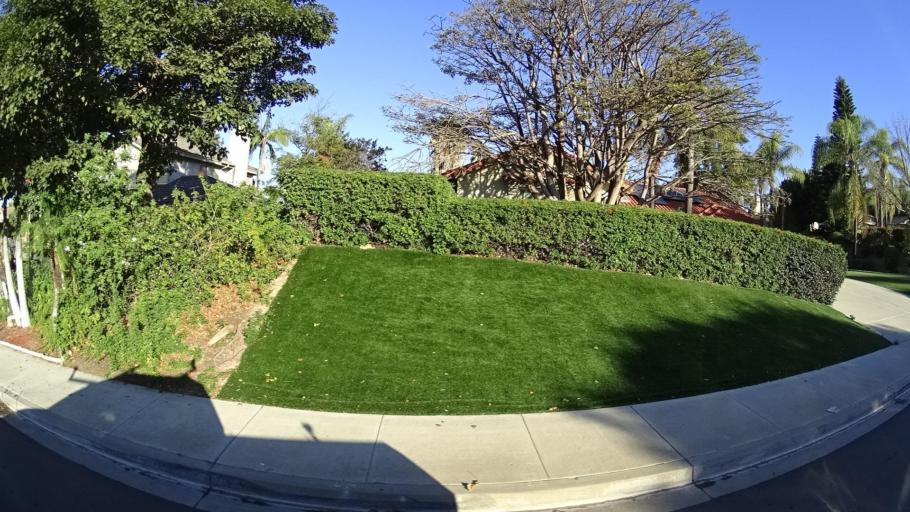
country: US
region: California
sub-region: San Diego County
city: Bonita
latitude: 32.6724
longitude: -117.0381
